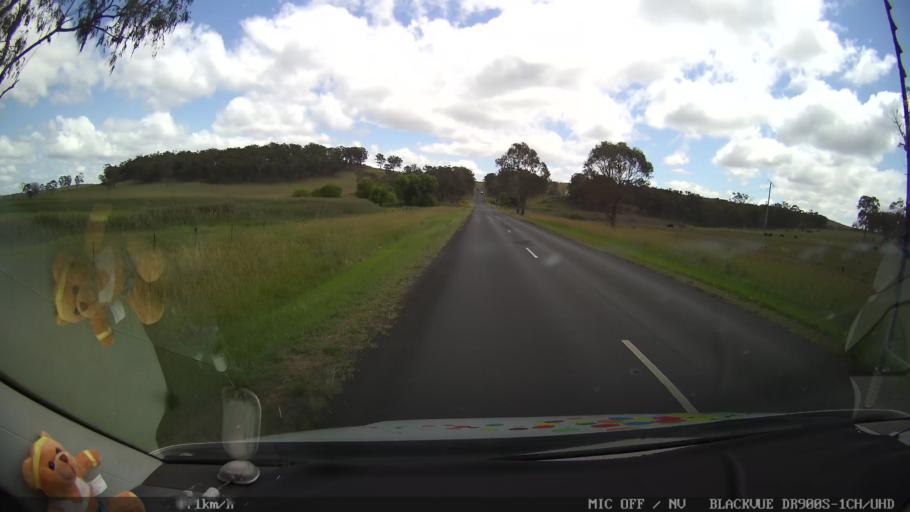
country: AU
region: New South Wales
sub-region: Glen Innes Severn
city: Glen Innes
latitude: -29.5963
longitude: 151.6664
